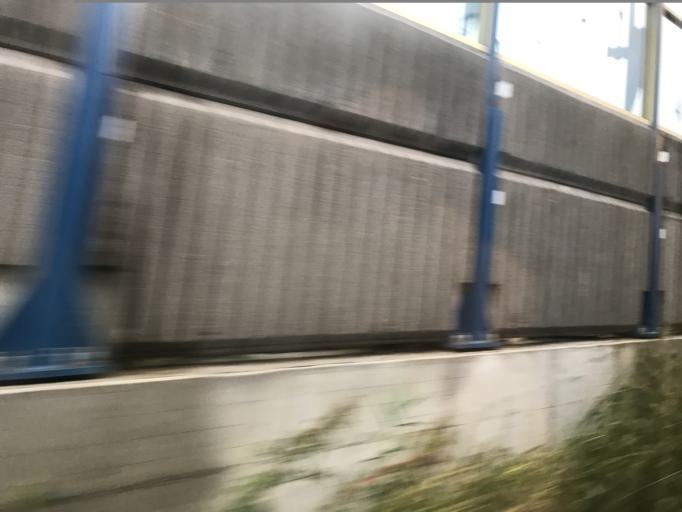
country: VA
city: Vatican City
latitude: 41.8589
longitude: 12.4593
